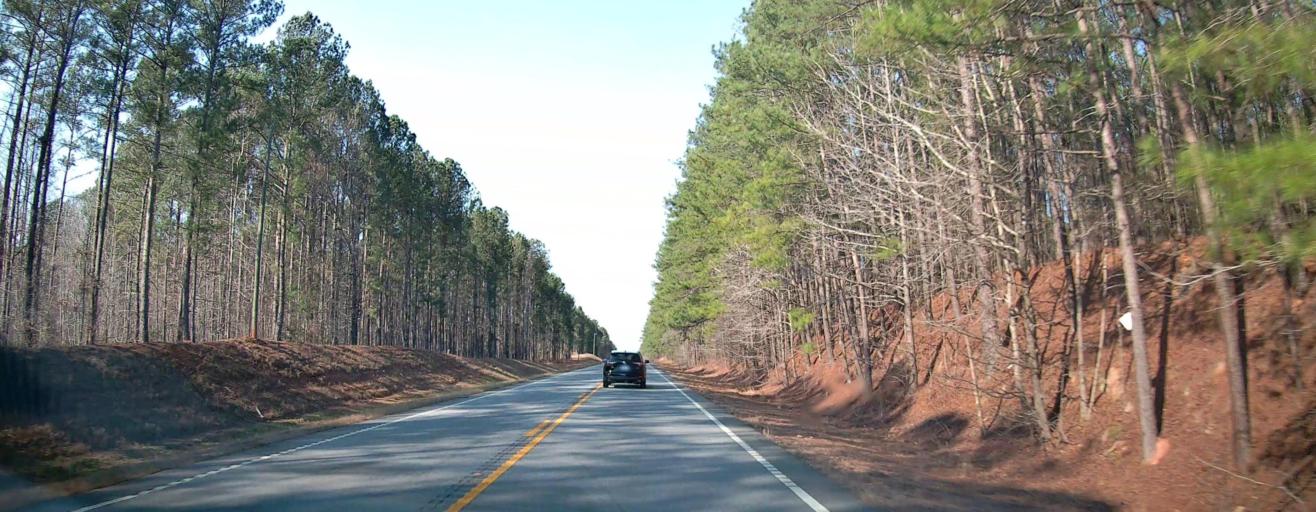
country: US
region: Georgia
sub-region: Butts County
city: Indian Springs
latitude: 33.1823
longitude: -83.8463
